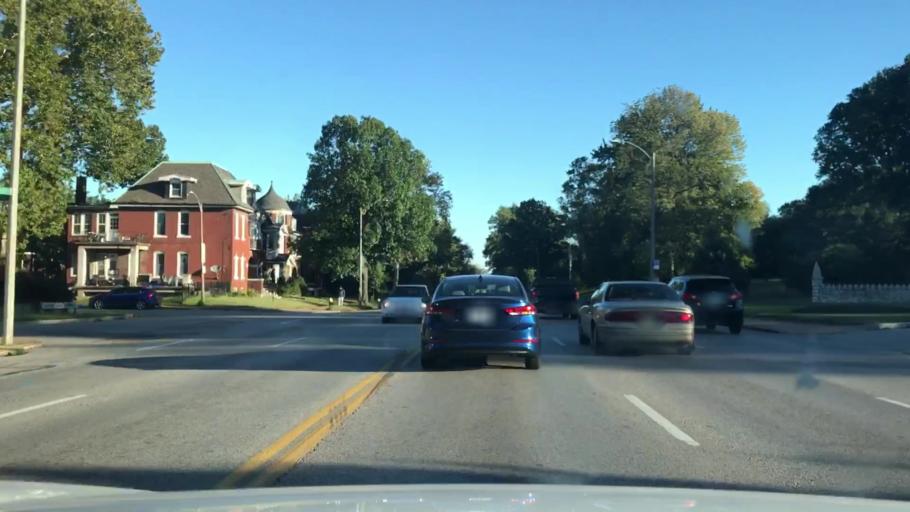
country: US
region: Missouri
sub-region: Saint Louis County
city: Richmond Heights
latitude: 38.6073
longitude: -90.2688
